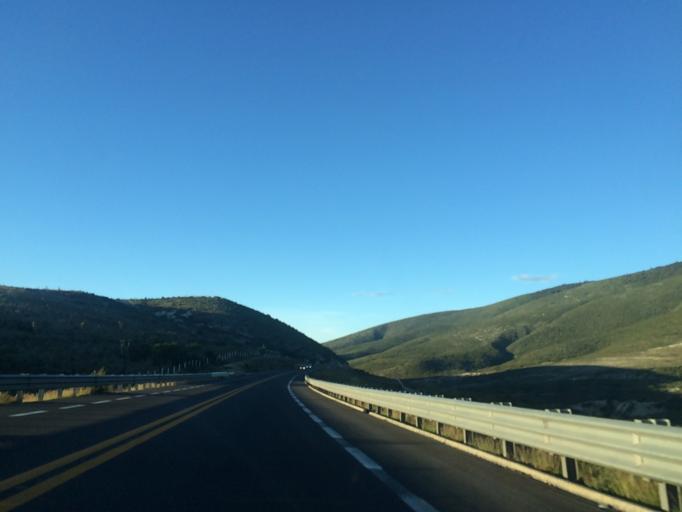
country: MX
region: Puebla
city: Morelos Canada
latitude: 18.6849
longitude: -97.4600
